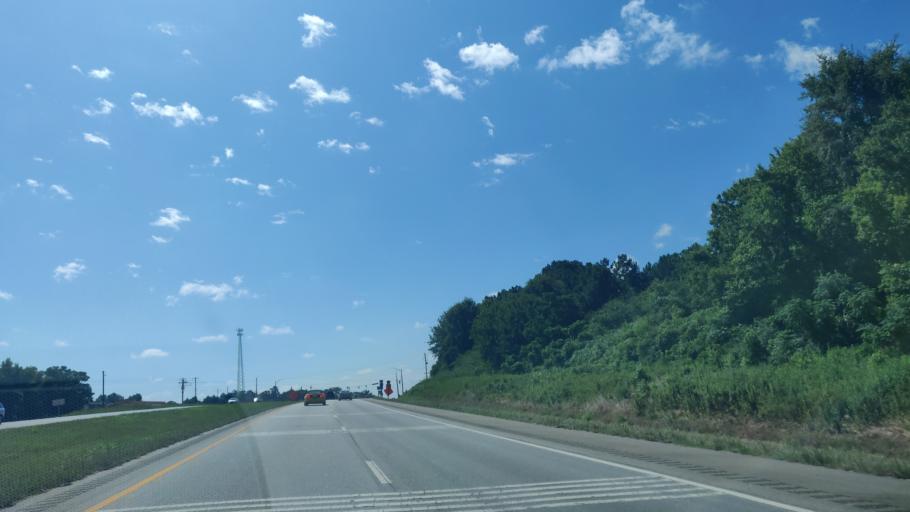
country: US
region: Alabama
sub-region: Lee County
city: Smiths Station
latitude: 32.5385
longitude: -85.0862
